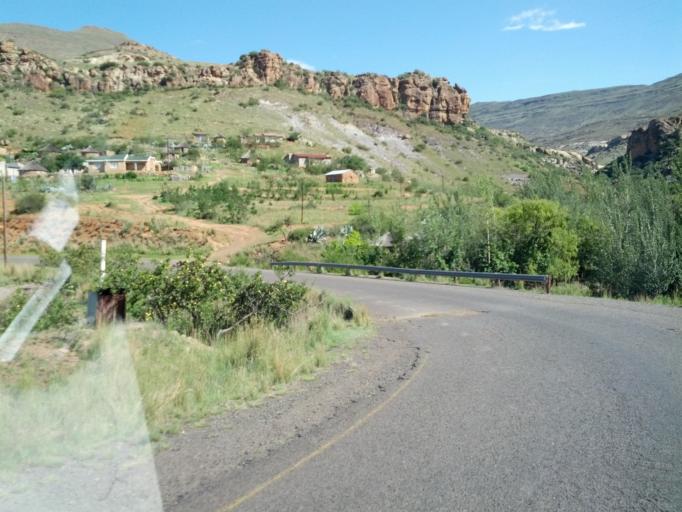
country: LS
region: Qacha's Nek
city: Qacha's Nek
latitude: -30.0735
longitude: 28.5600
